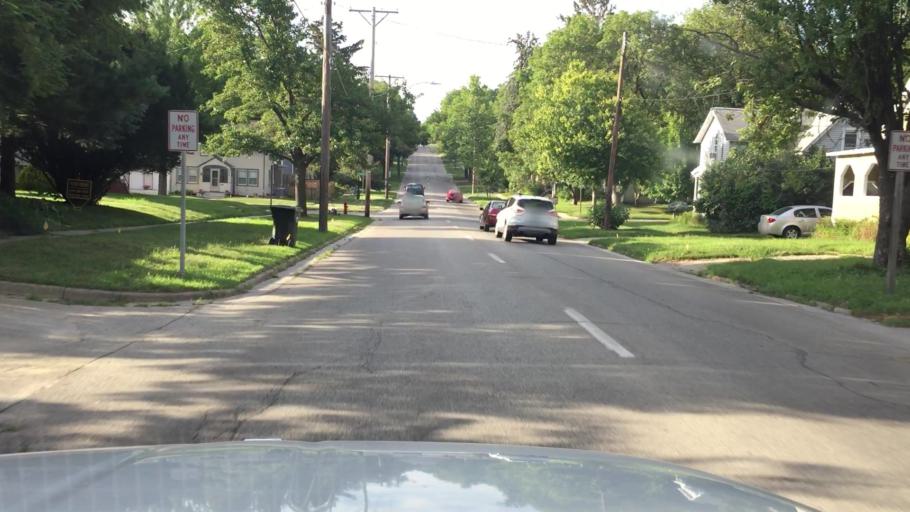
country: US
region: Iowa
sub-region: Johnson County
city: Iowa City
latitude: 41.6652
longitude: -91.5228
